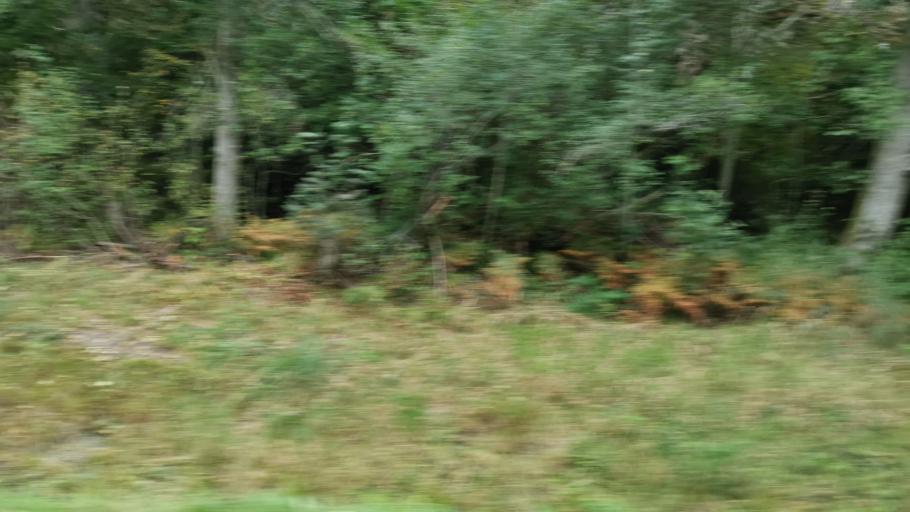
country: SE
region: Vaestra Goetaland
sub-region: Tanums Kommun
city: Tanumshede
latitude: 58.7049
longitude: 11.3360
